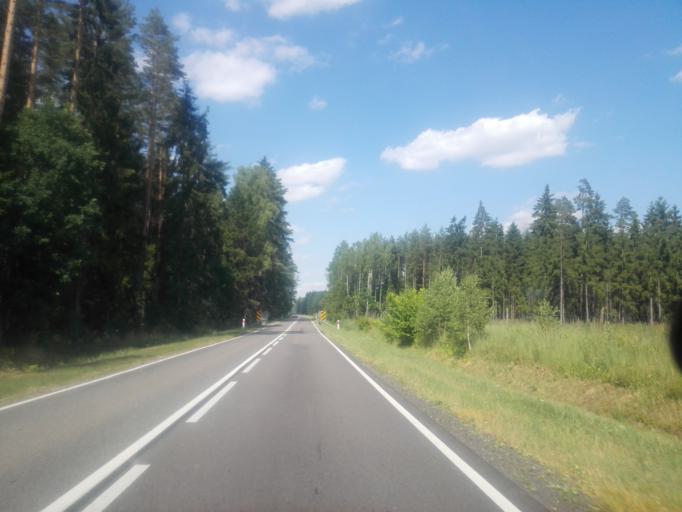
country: PL
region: Podlasie
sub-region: Powiat sejnenski
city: Sejny
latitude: 53.9938
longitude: 23.3080
